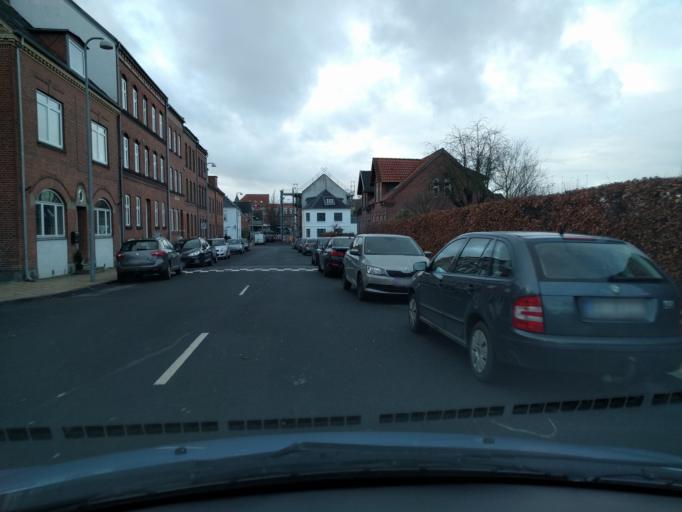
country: DK
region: South Denmark
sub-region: Odense Kommune
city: Odense
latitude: 55.4087
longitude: 10.3965
